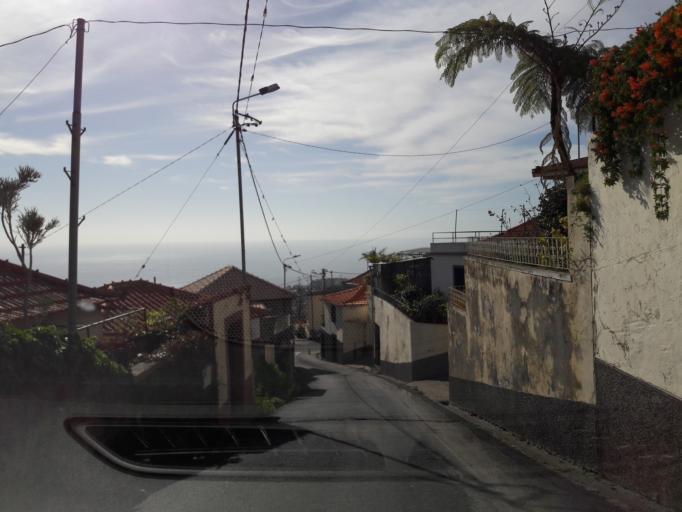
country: PT
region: Madeira
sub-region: Funchal
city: Nossa Senhora do Monte
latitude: 32.6683
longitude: -16.9215
